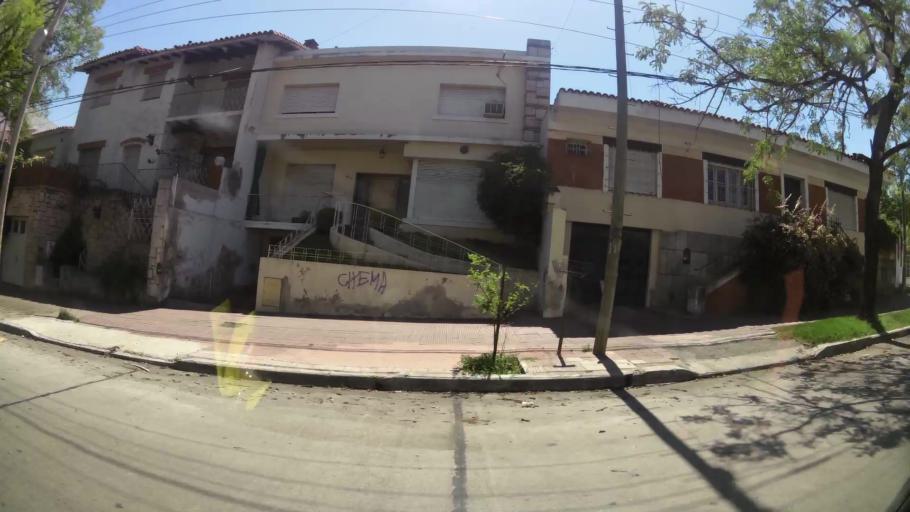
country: AR
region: Cordoba
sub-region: Departamento de Capital
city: Cordoba
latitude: -31.4029
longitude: -64.1873
